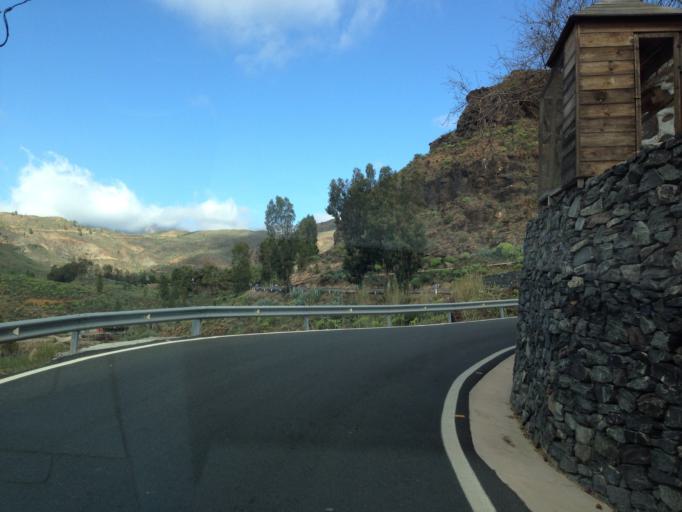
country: ES
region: Canary Islands
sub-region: Provincia de Las Palmas
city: Santa Lucia
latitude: 27.8915
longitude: -15.5633
